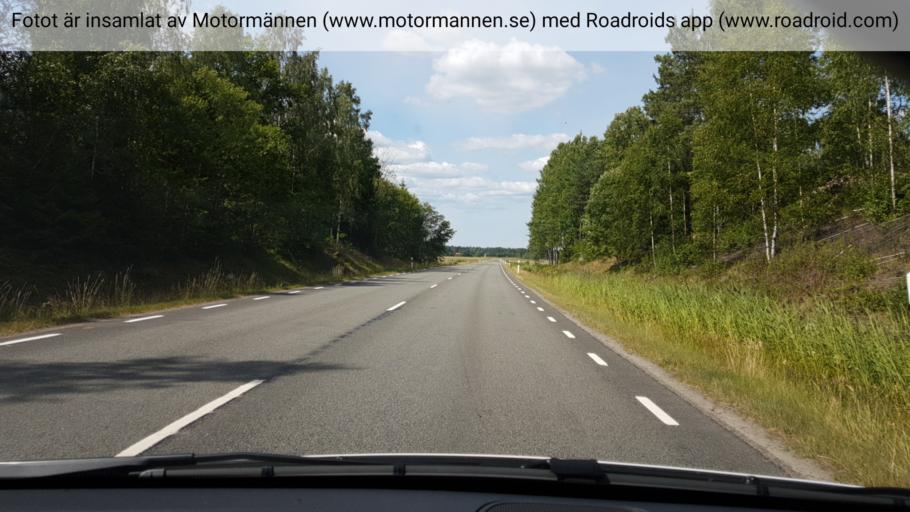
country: SE
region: Vaestra Goetaland
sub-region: Mariestads Kommun
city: Mariestad
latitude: 58.6189
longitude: 13.9535
